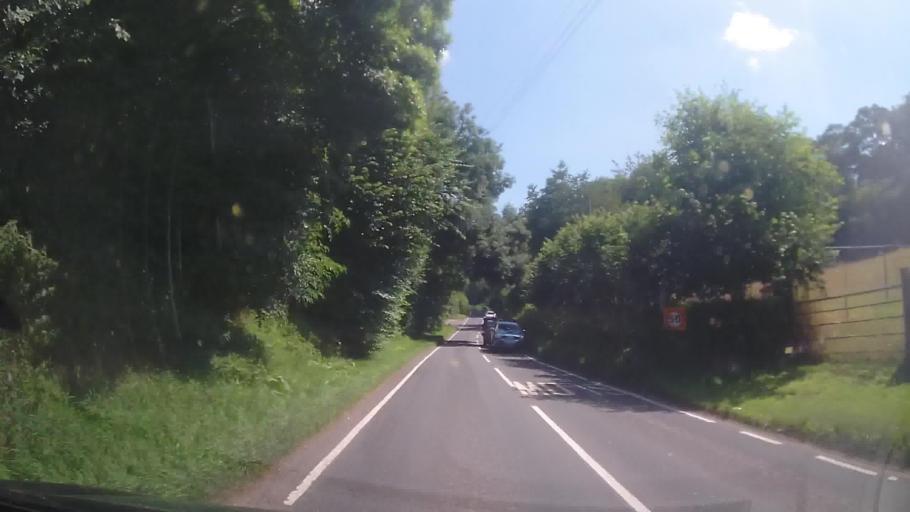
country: GB
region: England
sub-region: Herefordshire
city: Brockhampton
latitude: 51.9846
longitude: -2.5689
